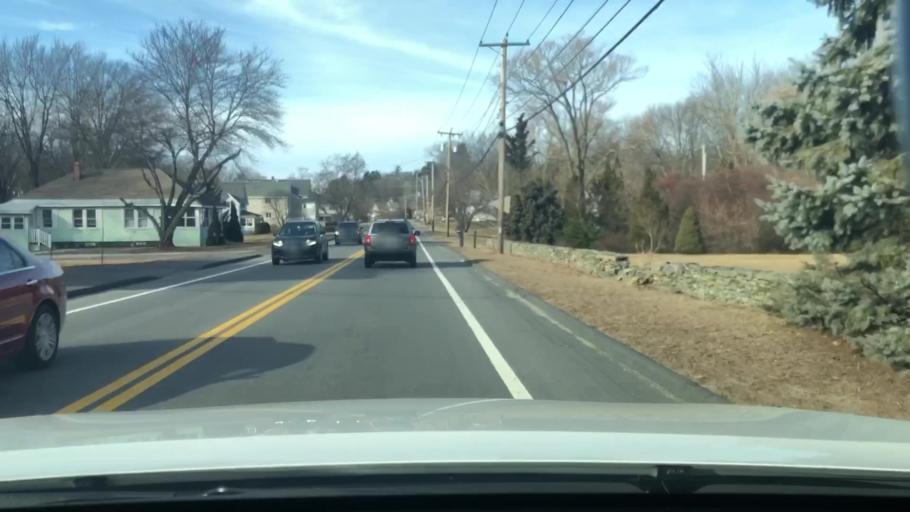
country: US
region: Massachusetts
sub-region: Worcester County
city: Millbury
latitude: 42.1992
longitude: -71.7711
